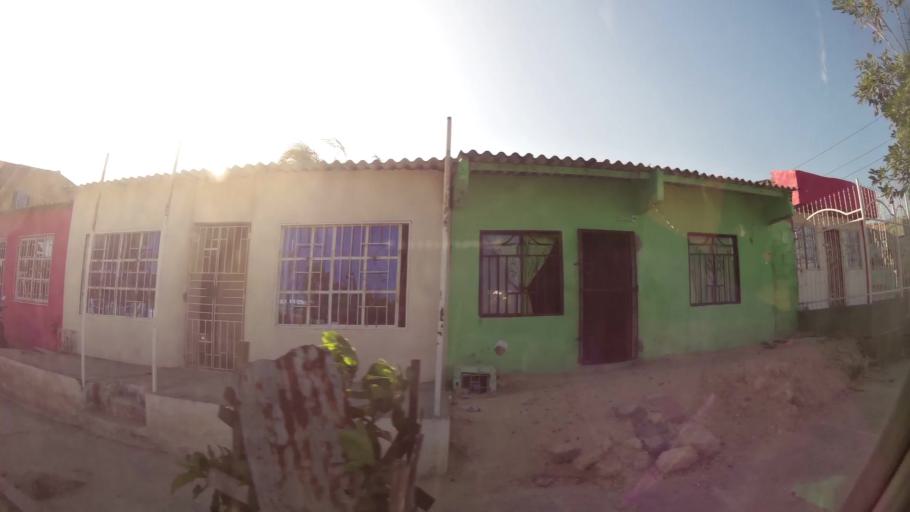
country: CO
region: Bolivar
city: Cartagena
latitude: 10.4143
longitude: -75.4957
